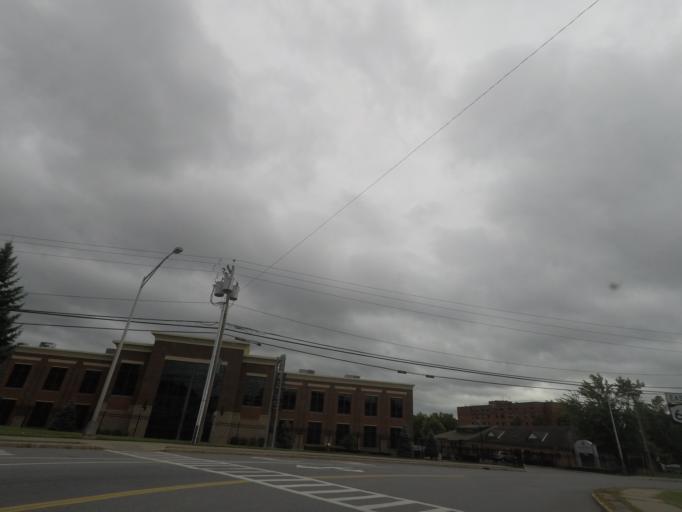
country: US
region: New York
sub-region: Saratoga County
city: Mechanicville
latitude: 42.9095
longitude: -73.6838
